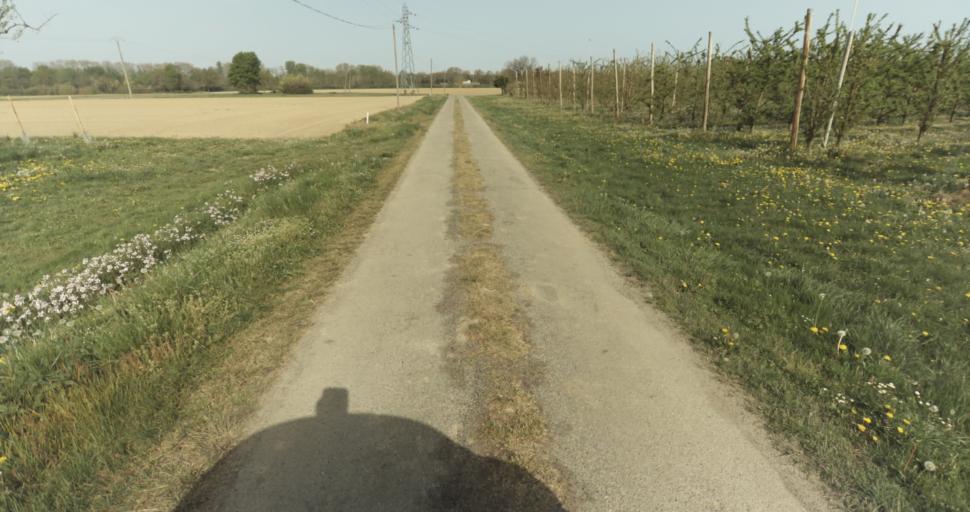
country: FR
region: Midi-Pyrenees
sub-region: Departement du Tarn-et-Garonne
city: Moissac
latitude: 44.0799
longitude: 1.1088
